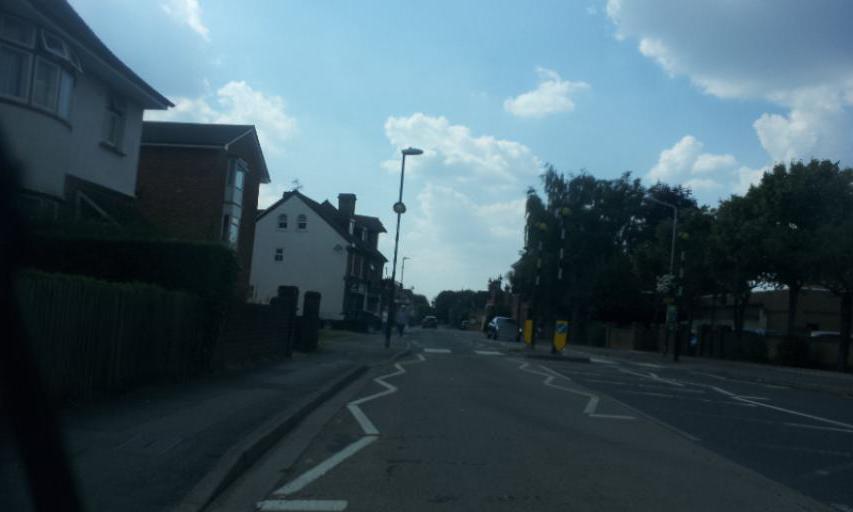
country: GB
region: England
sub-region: Kent
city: Paddock Wood
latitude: 51.1813
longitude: 0.3907
